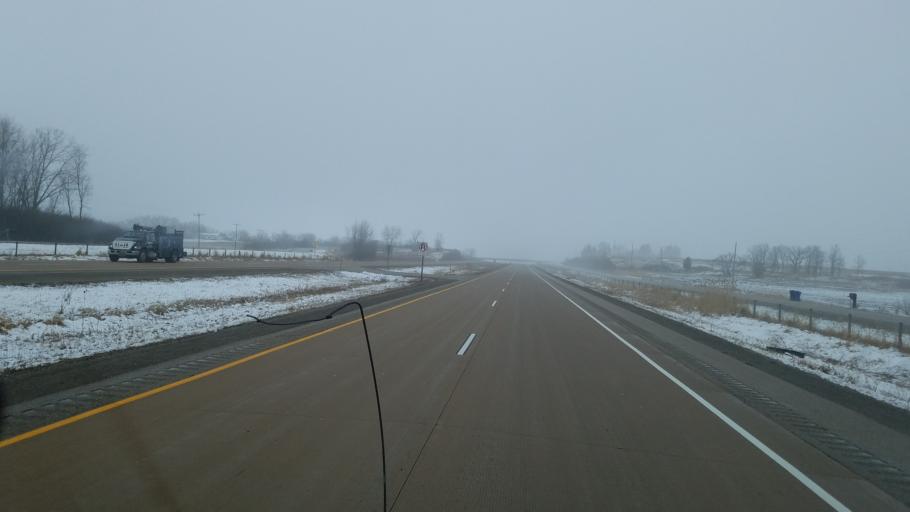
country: US
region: Wisconsin
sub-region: Winnebago County
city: Winneconne
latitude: 44.1473
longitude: -88.6640
